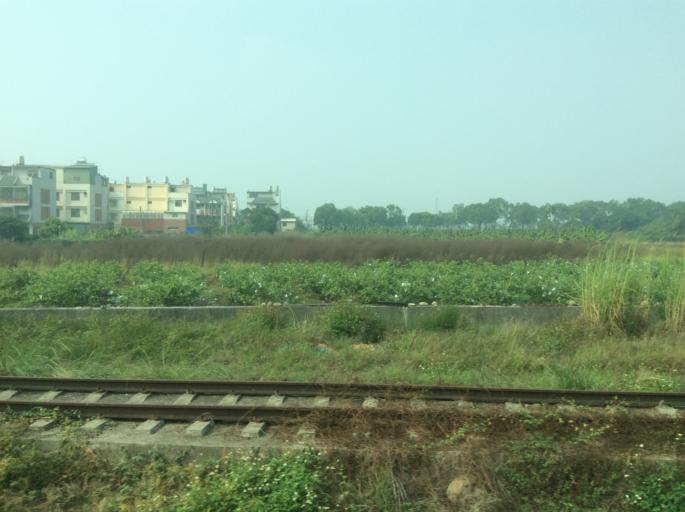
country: TW
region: Taiwan
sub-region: Yunlin
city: Douliu
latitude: 23.7618
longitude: 120.6171
